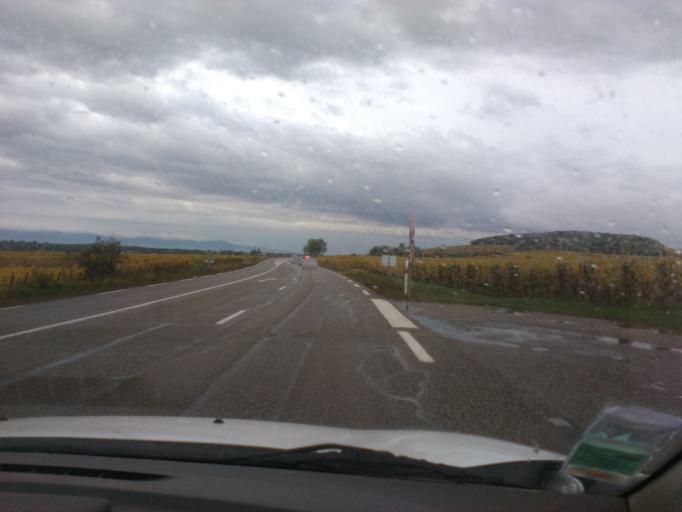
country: FR
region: Alsace
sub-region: Departement du Haut-Rhin
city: Ammerschwihr
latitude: 48.1157
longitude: 7.2901
